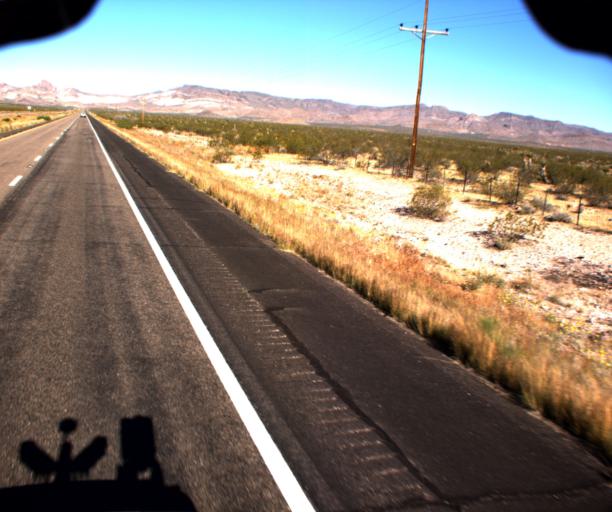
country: US
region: Arizona
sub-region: Mohave County
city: Golden Valley
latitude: 35.2270
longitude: -114.3159
